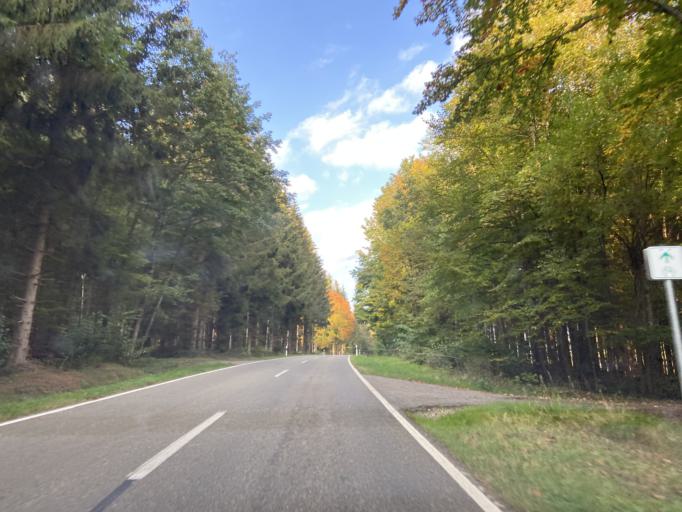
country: DE
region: Baden-Wuerttemberg
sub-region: Tuebingen Region
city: Scheer
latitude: 48.0805
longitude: 9.3055
